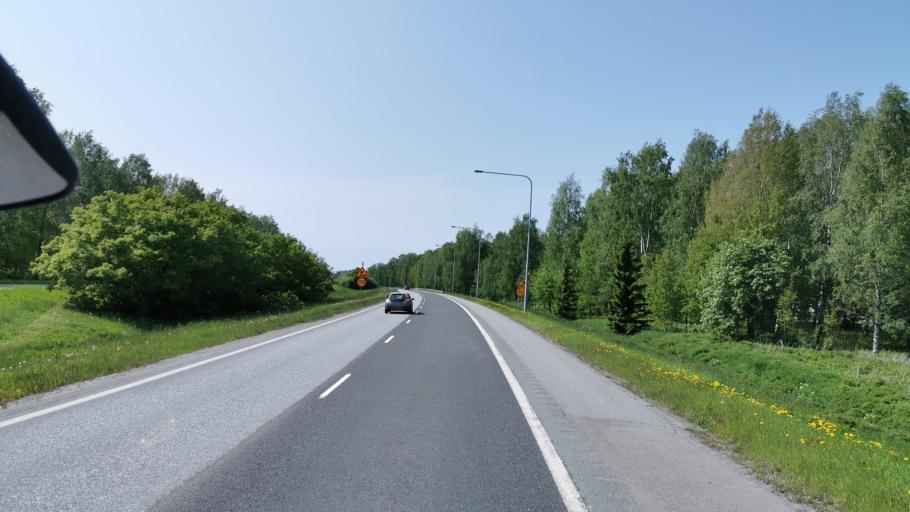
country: FI
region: Ostrobothnia
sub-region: Vaasa
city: Teeriniemi
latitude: 63.0783
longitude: 21.6637
